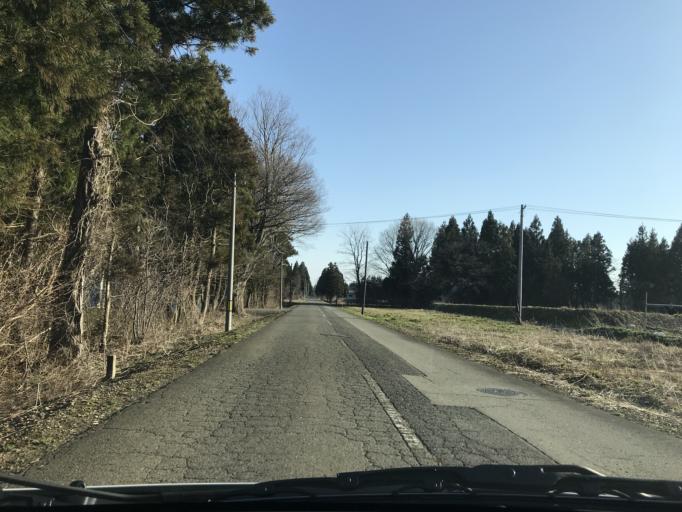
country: JP
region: Iwate
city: Kitakami
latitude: 39.2480
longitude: 141.0399
